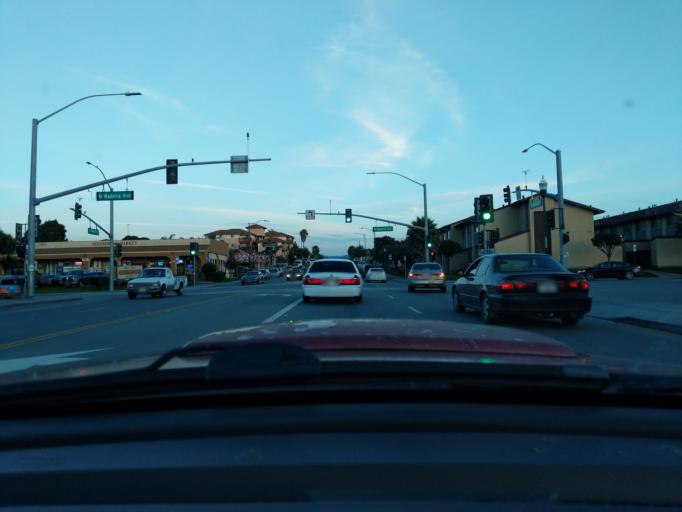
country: US
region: California
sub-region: Monterey County
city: Salinas
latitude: 36.6772
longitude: -121.6384
